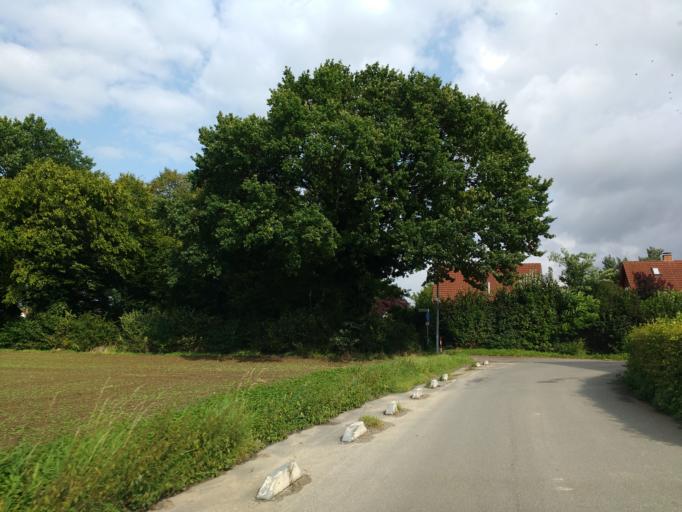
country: DE
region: North Rhine-Westphalia
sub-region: Regierungsbezirk Detmold
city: Lemgo
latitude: 52.0151
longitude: 8.8868
